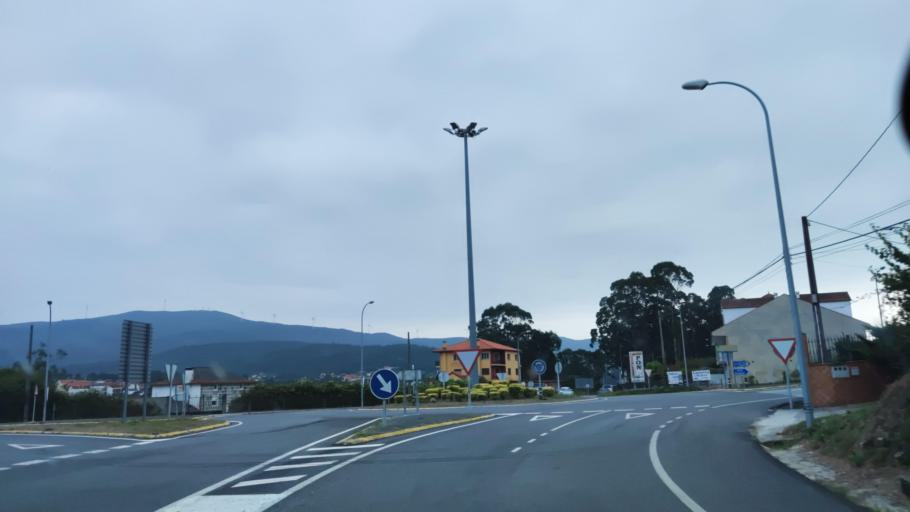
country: ES
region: Galicia
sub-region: Provincia de Pontevedra
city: Catoira
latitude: 42.6775
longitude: -8.7295
